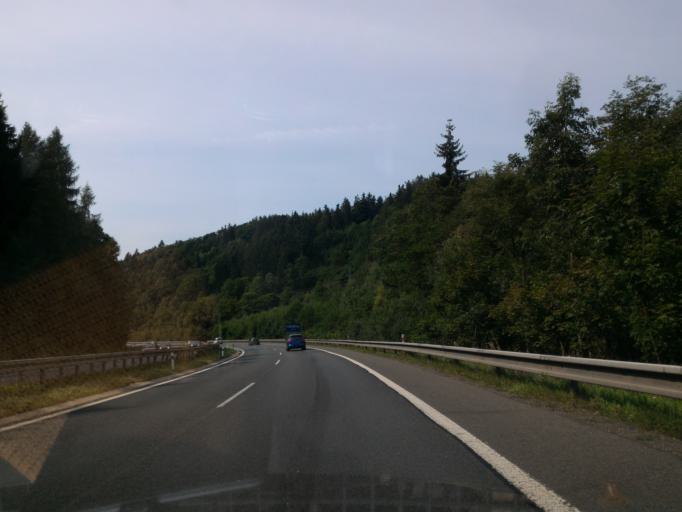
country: CZ
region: Liberecky
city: Hodkovice nad Mohelkou
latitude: 50.6835
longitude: 15.1021
